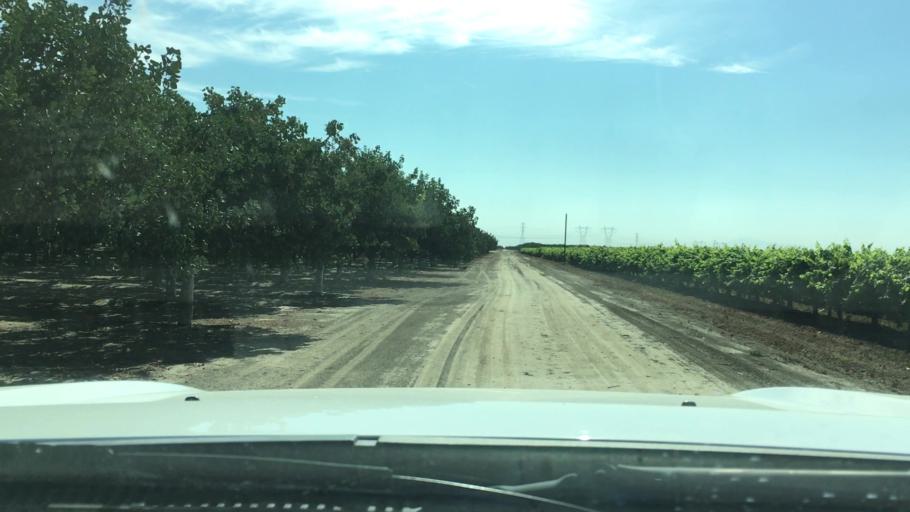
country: US
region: California
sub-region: Kern County
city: Buttonwillow
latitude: 35.3658
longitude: -119.3903
